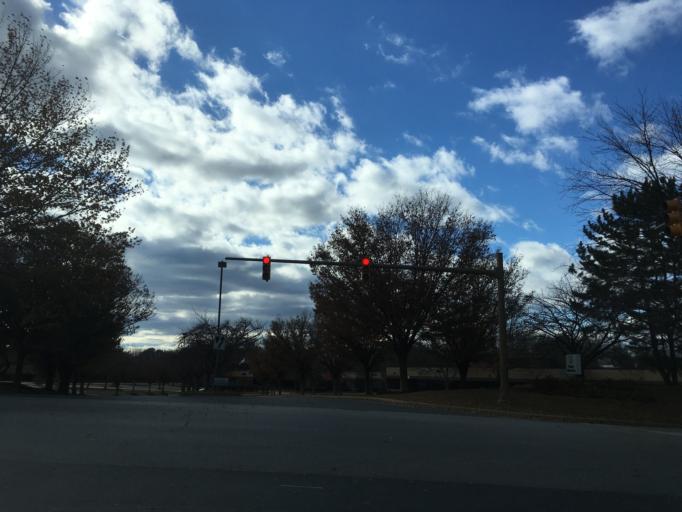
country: US
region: Maryland
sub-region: Howard County
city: Columbia
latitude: 39.1940
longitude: -76.8201
